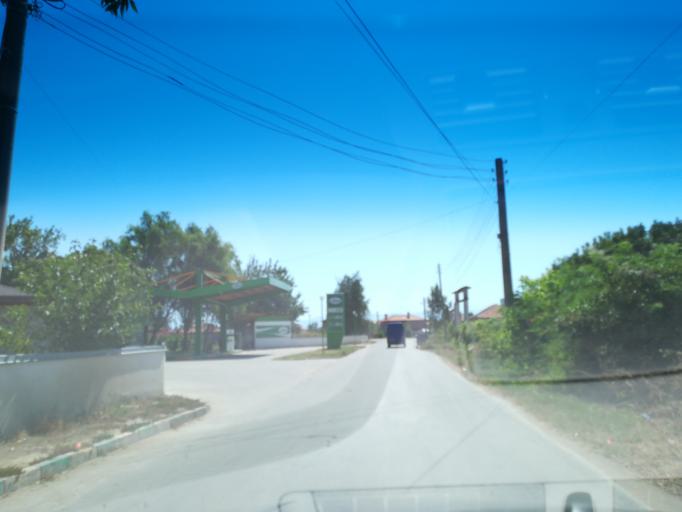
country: BG
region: Pazardzhik
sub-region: Obshtina Pazardzhik
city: Pazardzhik
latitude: 42.2727
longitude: 24.3967
